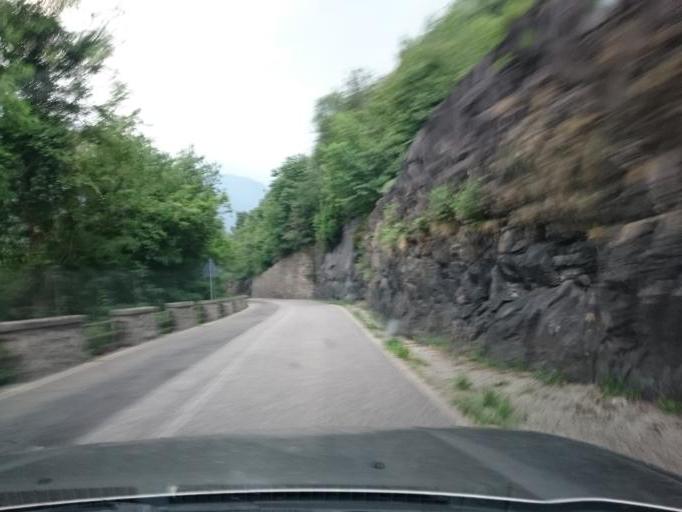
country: IT
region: Lombardy
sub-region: Provincia di Brescia
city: Cimbergo
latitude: 46.0284
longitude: 10.3649
